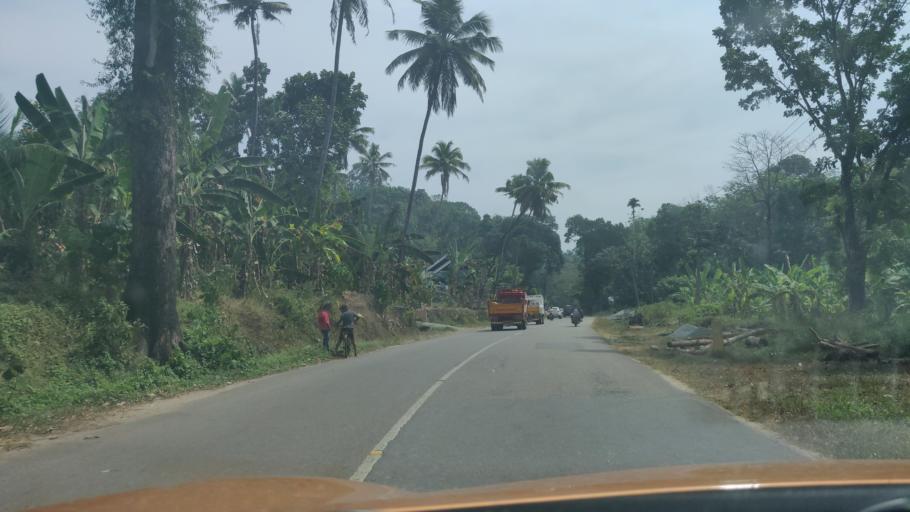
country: IN
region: Kerala
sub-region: Ernakulam
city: Muvattupuzha
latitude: 9.8852
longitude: 76.6496
